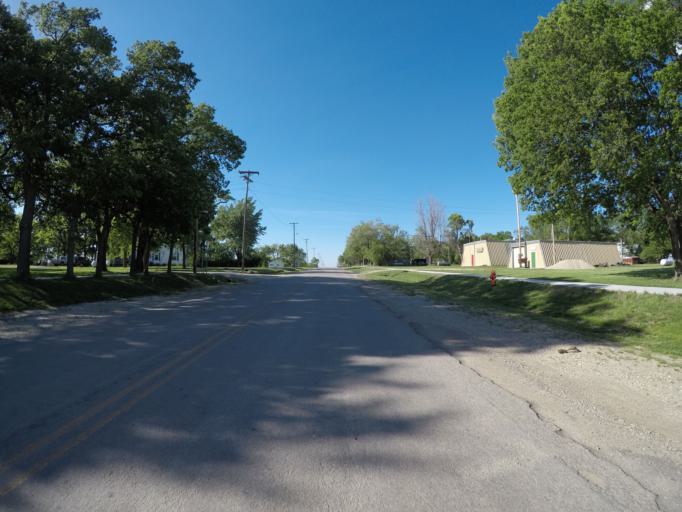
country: US
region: Kansas
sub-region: Clay County
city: Clay Center
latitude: 39.4315
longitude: -96.9983
